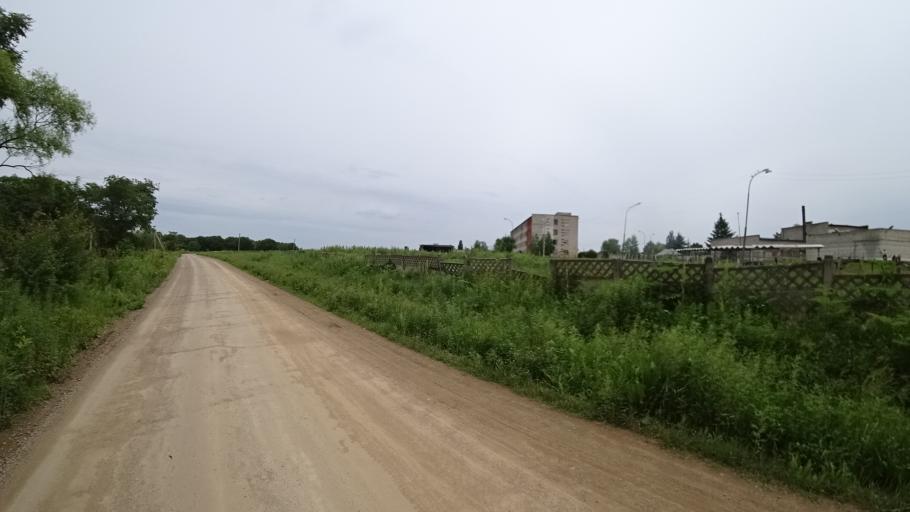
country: RU
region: Primorskiy
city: Arsen'yev
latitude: 44.1997
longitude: 133.3101
